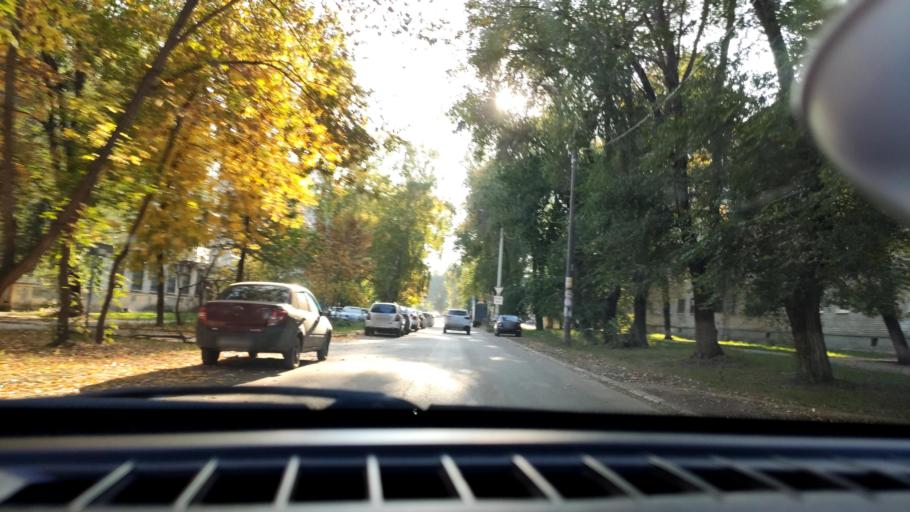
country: RU
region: Samara
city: Petra-Dubrava
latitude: 53.2296
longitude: 50.2761
